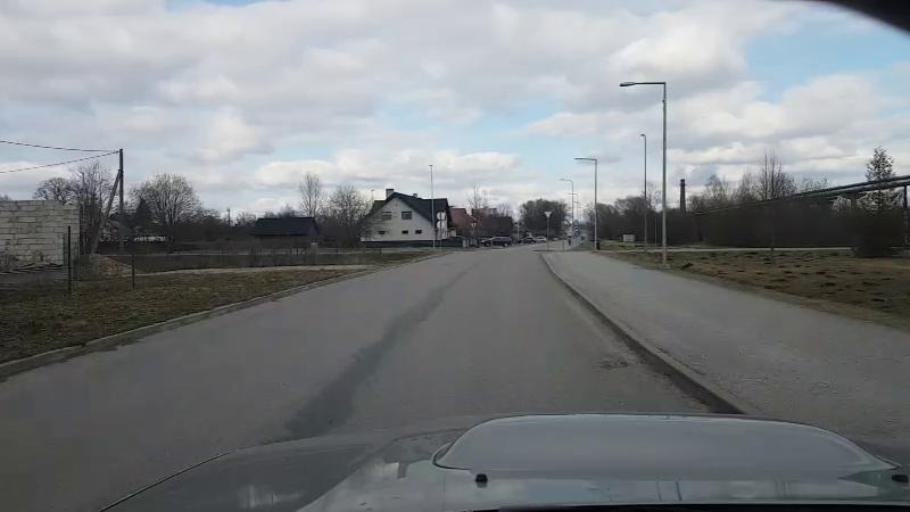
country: EE
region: Jaervamaa
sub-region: Paide linn
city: Paide
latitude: 58.8827
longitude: 25.5492
